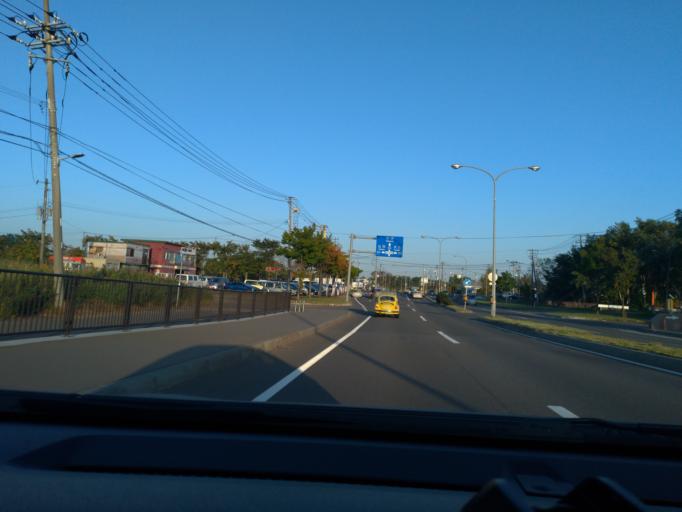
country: JP
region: Hokkaido
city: Ishikari
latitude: 43.1571
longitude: 141.4121
